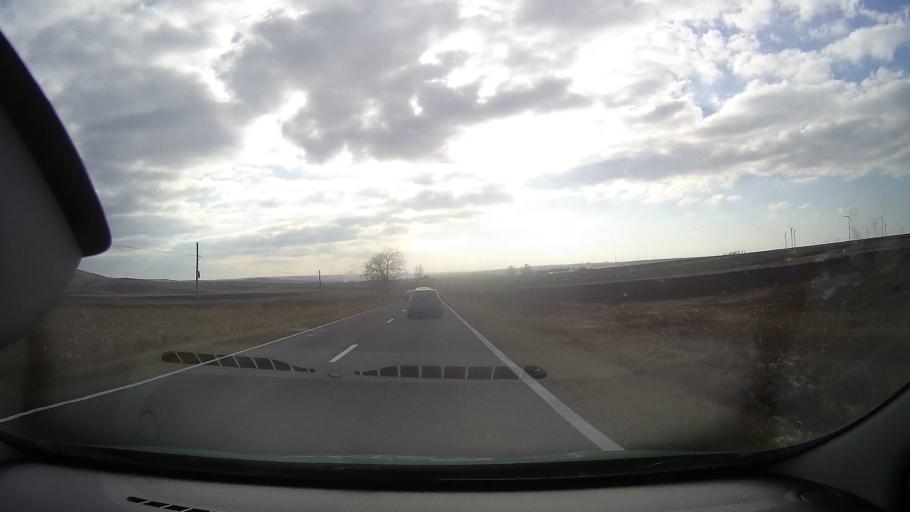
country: RO
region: Tulcea
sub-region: Comuna Topolog
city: Topolog
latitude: 44.8928
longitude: 28.3952
